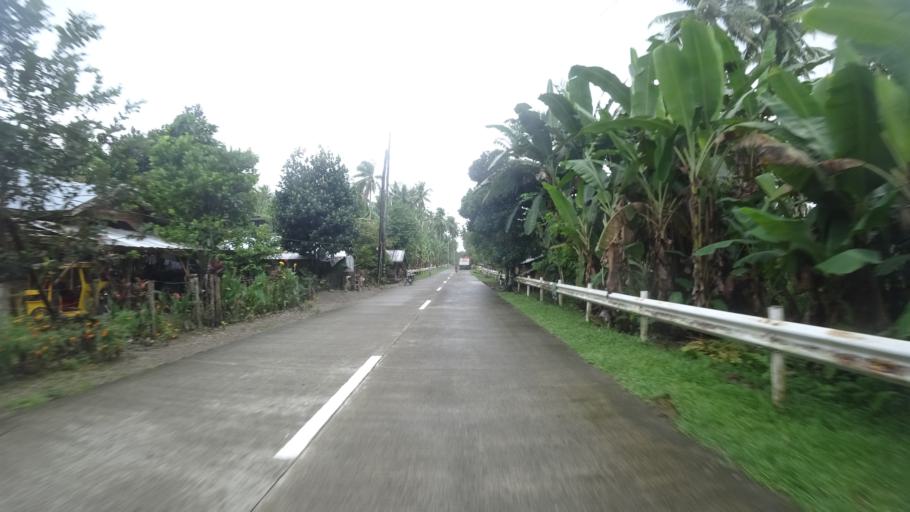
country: PH
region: Eastern Visayas
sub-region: Province of Leyte
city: Bugho
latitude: 10.8292
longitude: 124.9362
